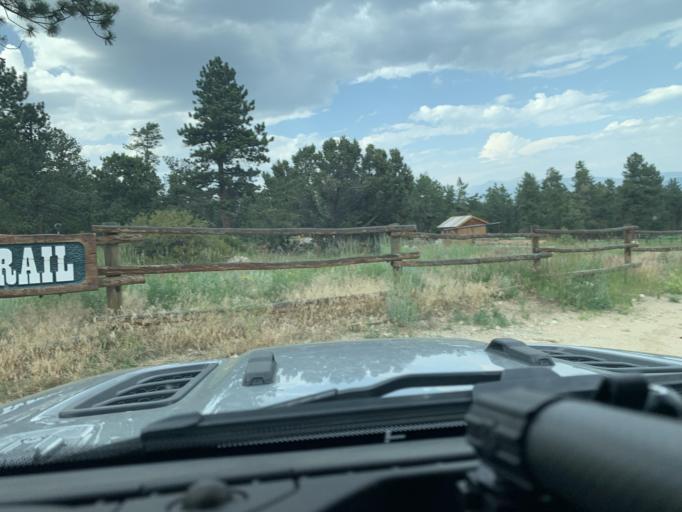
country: US
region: Colorado
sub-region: Chaffee County
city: Buena Vista
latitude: 38.7400
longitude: -106.1761
